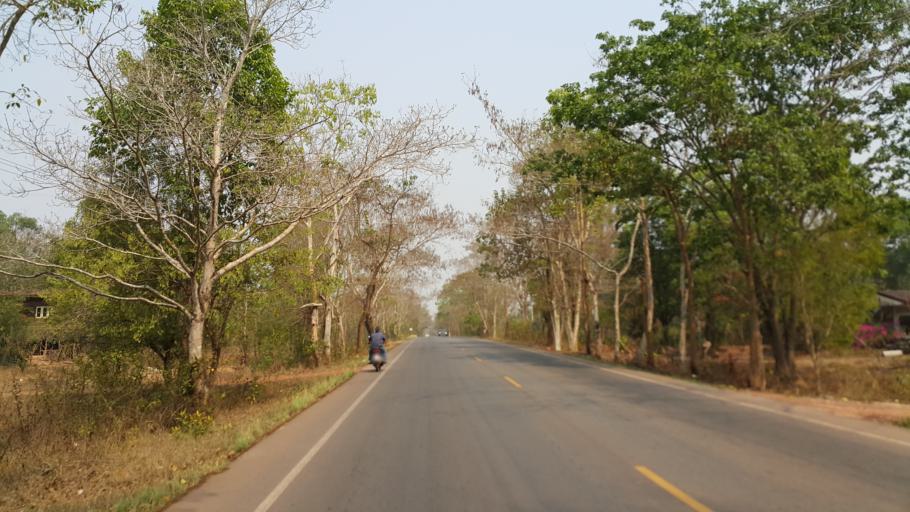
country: TH
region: Nakhon Phanom
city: Ban Phaeng
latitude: 17.8420
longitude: 104.2636
